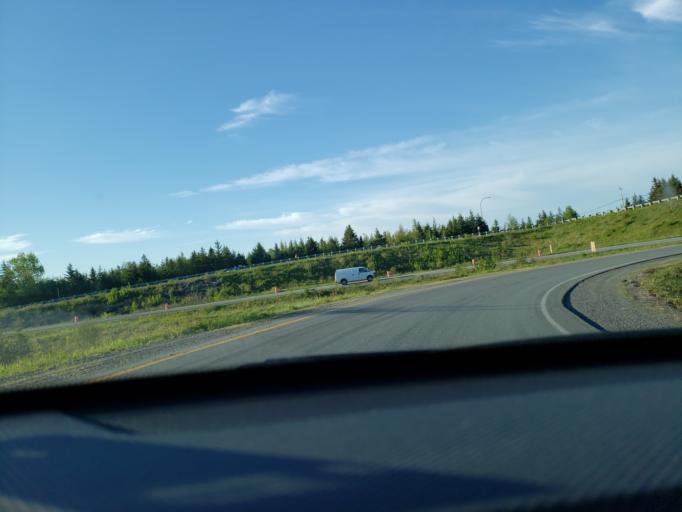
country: CA
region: Nova Scotia
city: Cole Harbour
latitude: 44.7139
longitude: -63.3928
